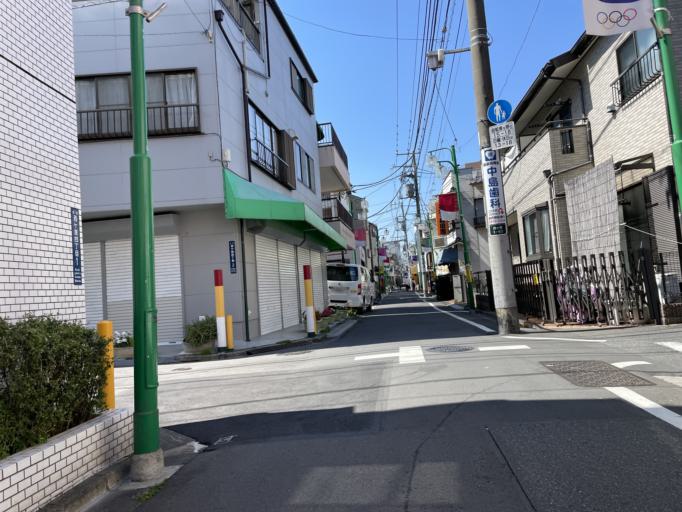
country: JP
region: Saitama
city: Kawaguchi
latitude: 35.7423
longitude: 139.7400
